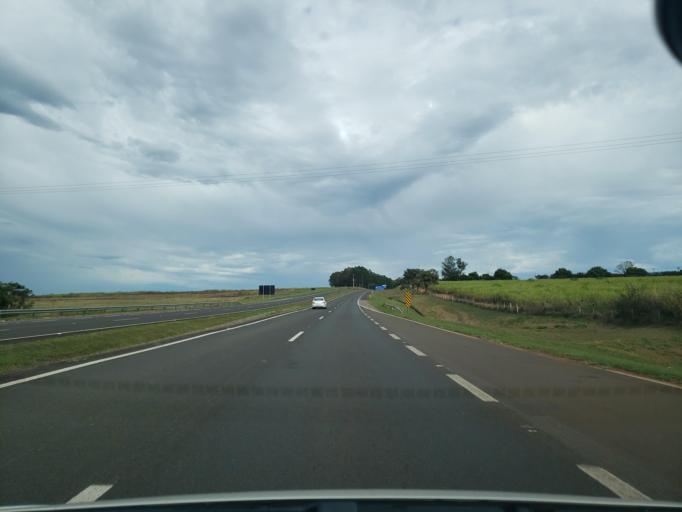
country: BR
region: Sao Paulo
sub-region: Dois Corregos
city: Dois Corregos
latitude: -22.2659
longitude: -48.3835
